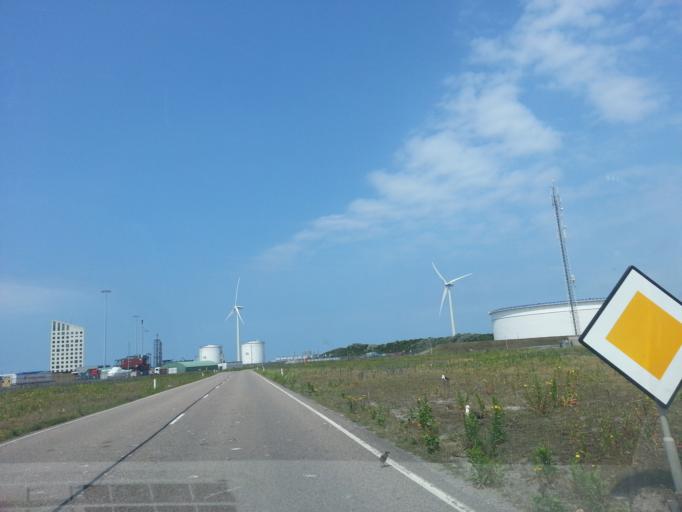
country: NL
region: South Holland
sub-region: Gemeente Rotterdam
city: Hoek van Holland
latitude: 51.9754
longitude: 4.0467
